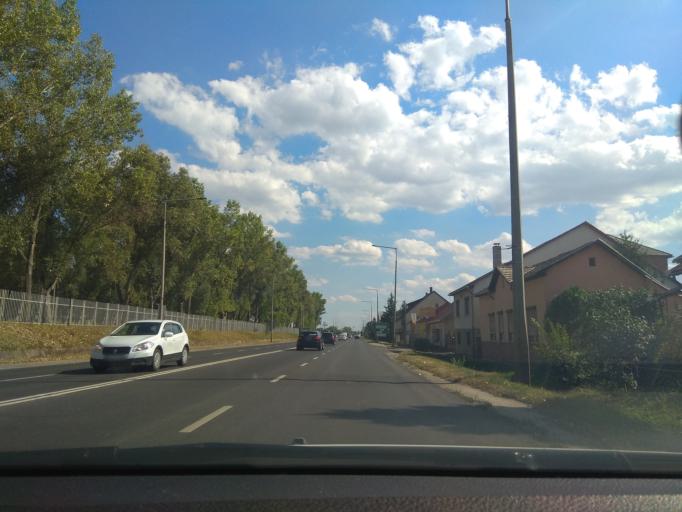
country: HU
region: Borsod-Abauj-Zemplen
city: Miskolc
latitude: 48.0645
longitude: 20.7933
